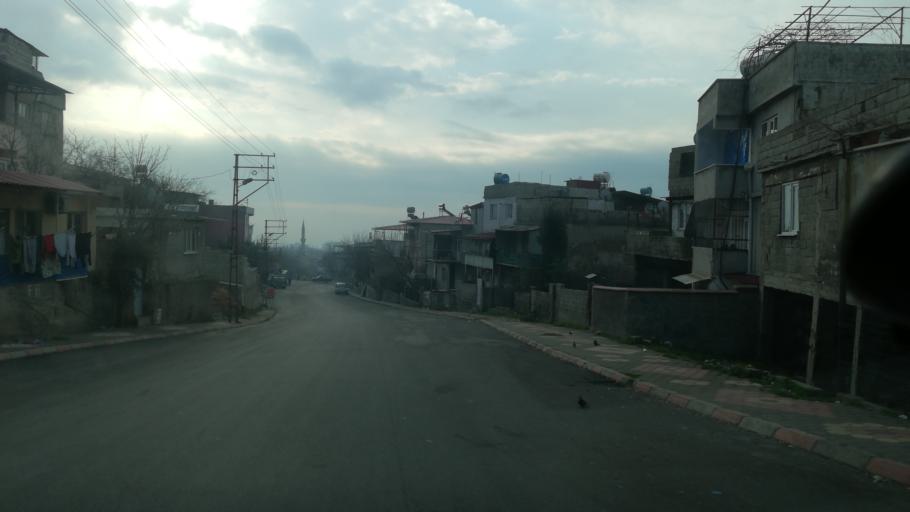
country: TR
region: Kahramanmaras
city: Kahramanmaras
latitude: 37.5917
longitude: 36.9070
